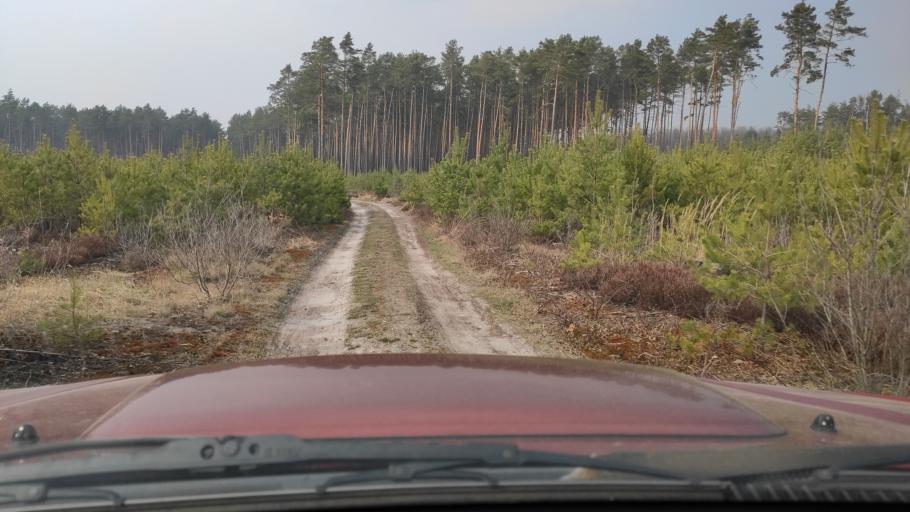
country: PL
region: Masovian Voivodeship
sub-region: Powiat zwolenski
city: Zwolen
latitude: 51.3939
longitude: 21.5726
